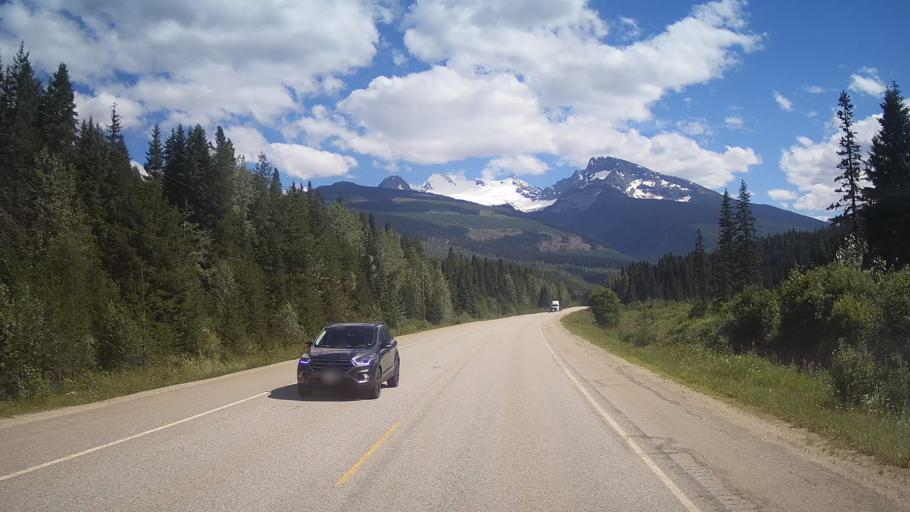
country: CA
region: Alberta
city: Jasper Park Lodge
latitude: 52.5949
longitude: -119.1021
